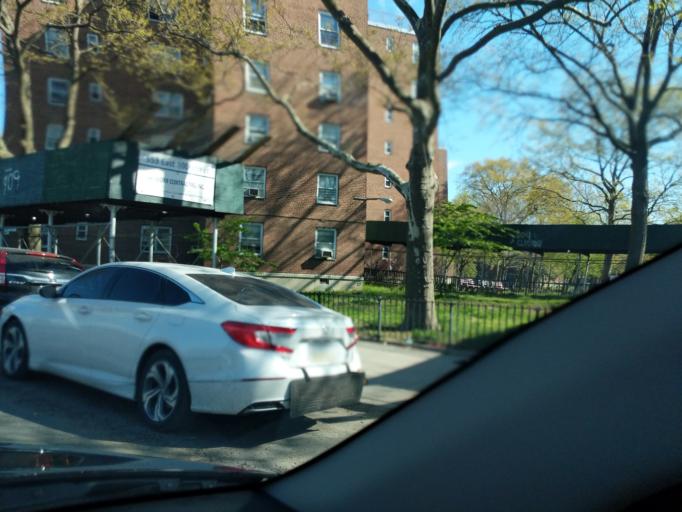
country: US
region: New York
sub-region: Kings County
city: East New York
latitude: 40.6523
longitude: -73.8963
